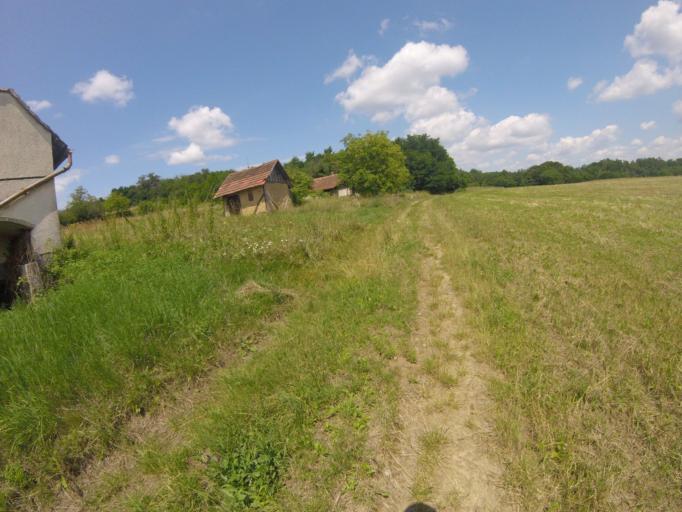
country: HU
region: Zala
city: Nagykanizsa
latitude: 46.5550
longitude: 17.0279
